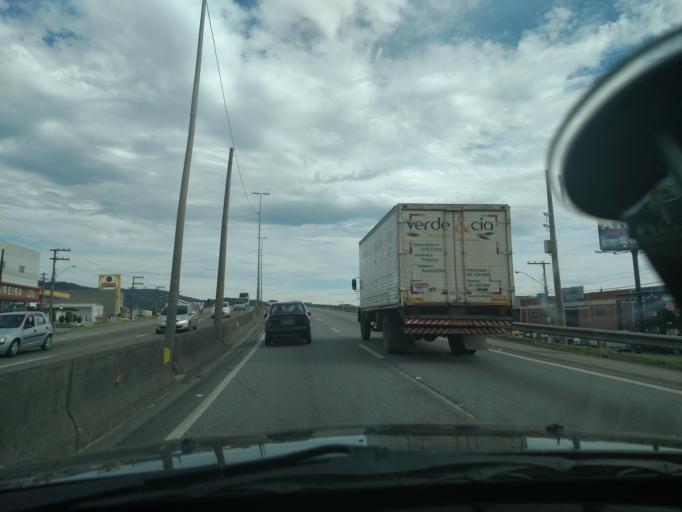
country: BR
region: Santa Catarina
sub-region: Biguacu
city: Biguacu
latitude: -27.5391
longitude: -48.6238
